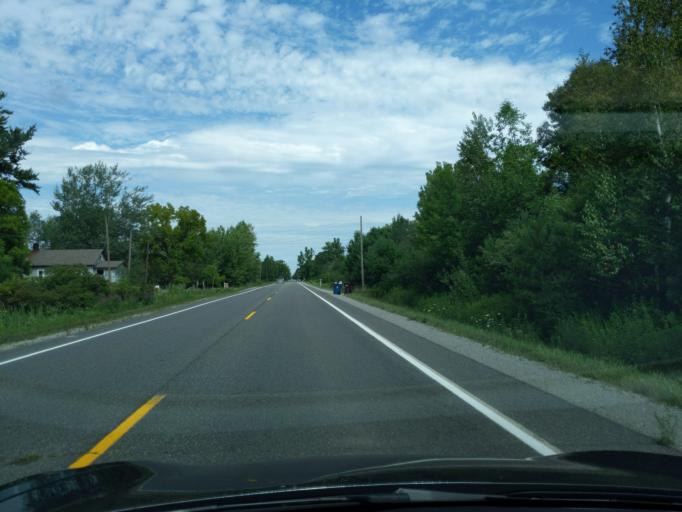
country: US
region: Michigan
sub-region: Midland County
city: Midland
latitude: 43.5761
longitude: -84.3695
